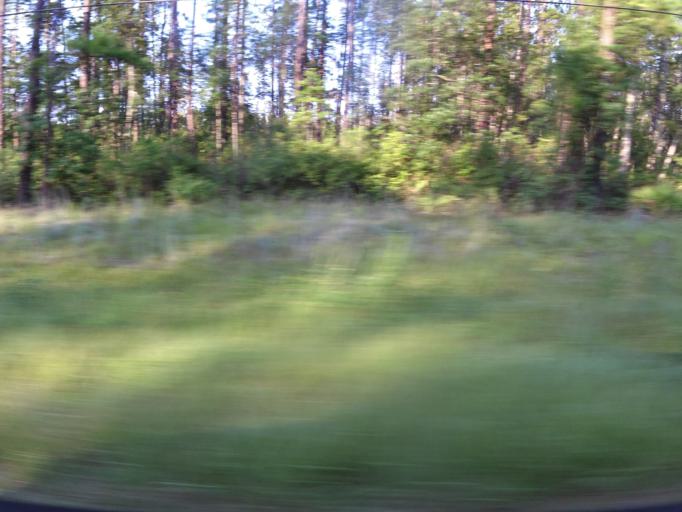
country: US
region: Florida
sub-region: Duval County
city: Baldwin
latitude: 30.3862
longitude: -82.0227
